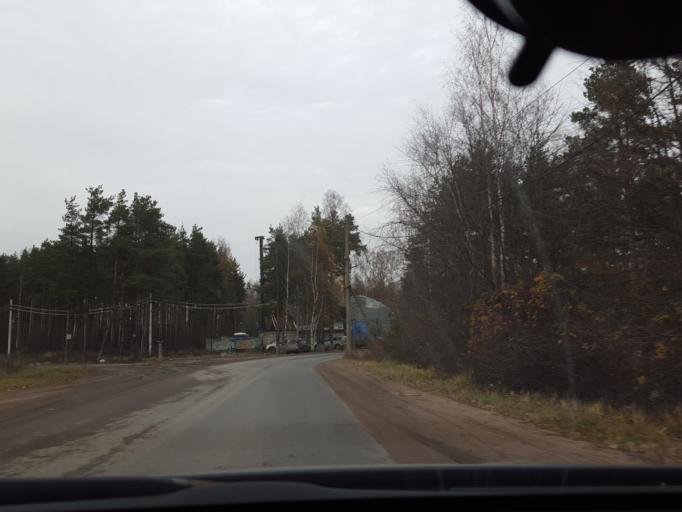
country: RU
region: St.-Petersburg
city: Shuvalovo
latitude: 60.0456
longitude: 30.2678
